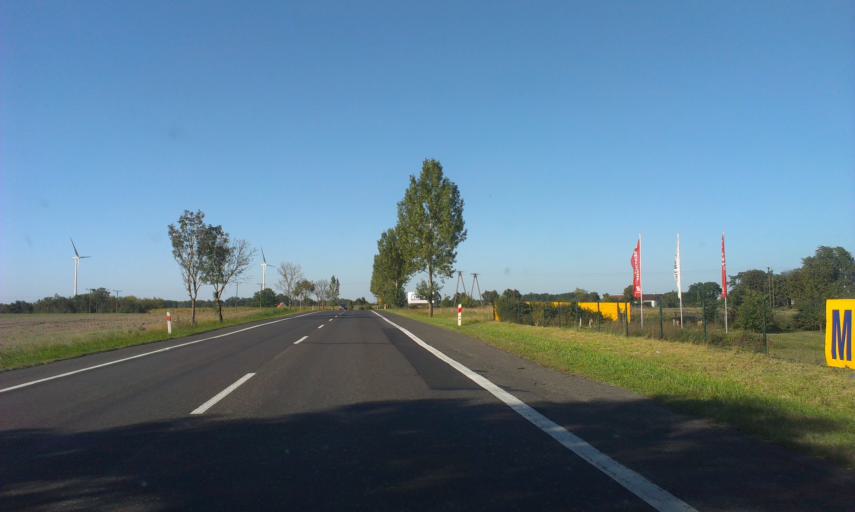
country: PL
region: Kujawsko-Pomorskie
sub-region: Powiat torunski
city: Chelmza
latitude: 53.1914
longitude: 18.5650
